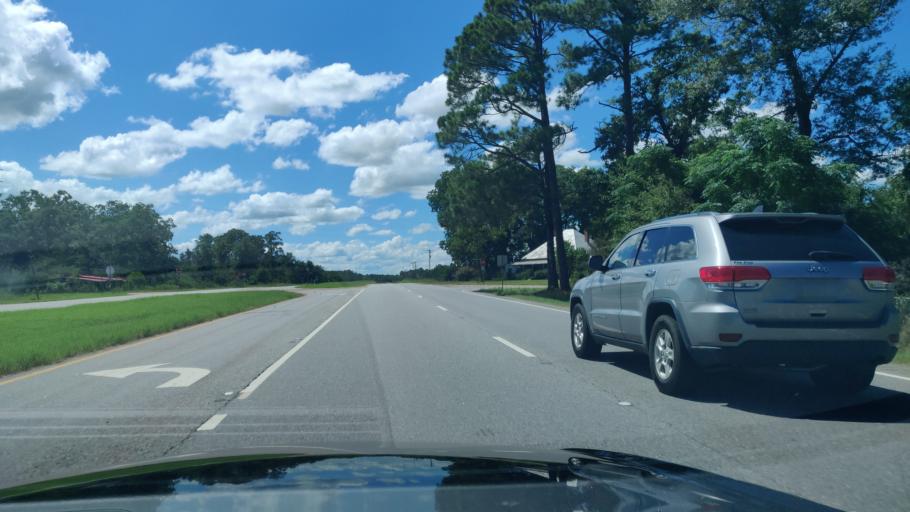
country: US
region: Georgia
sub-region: Webster County
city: Preston
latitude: 31.9191
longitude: -84.5436
